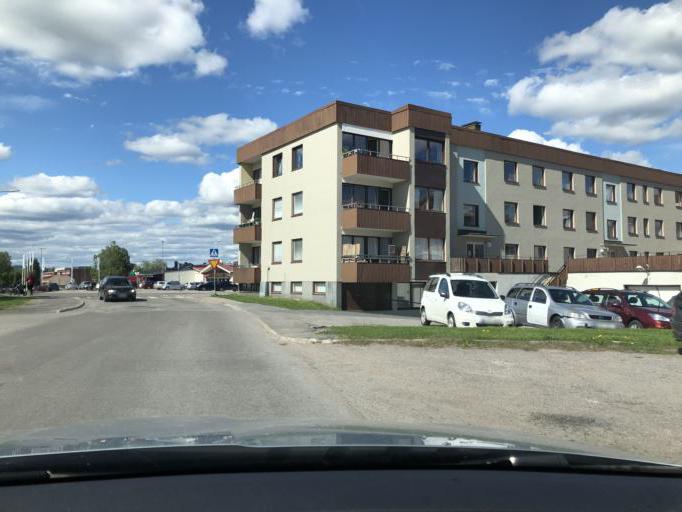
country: SE
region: Norrbotten
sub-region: Alvsbyns Kommun
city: AElvsbyn
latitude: 65.6715
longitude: 21.0114
